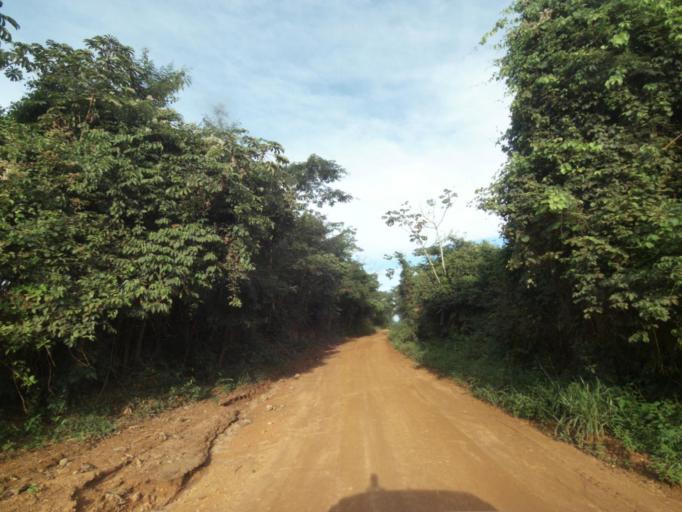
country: BR
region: Goias
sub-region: Jaragua
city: Jaragua
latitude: -15.8893
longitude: -49.4738
